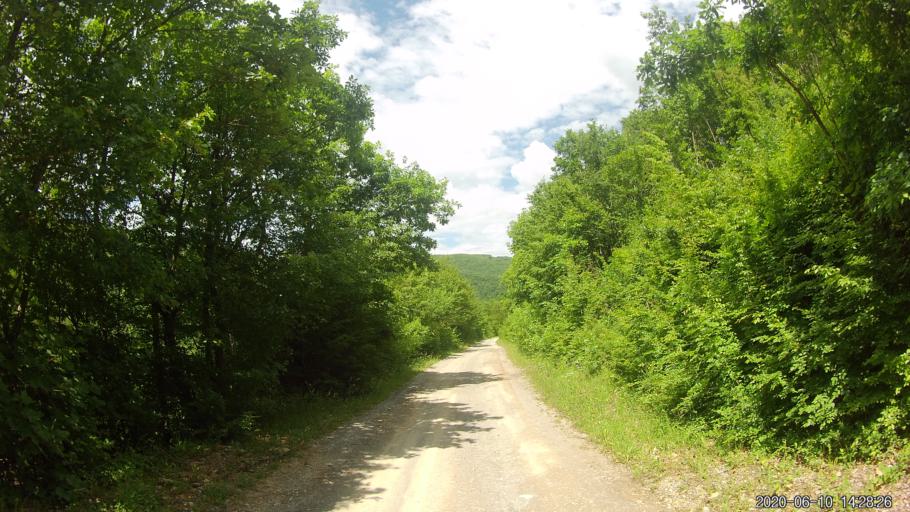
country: XK
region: Prizren
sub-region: Komuna e Therandes
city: Budakovo
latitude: 42.4125
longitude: 20.9143
